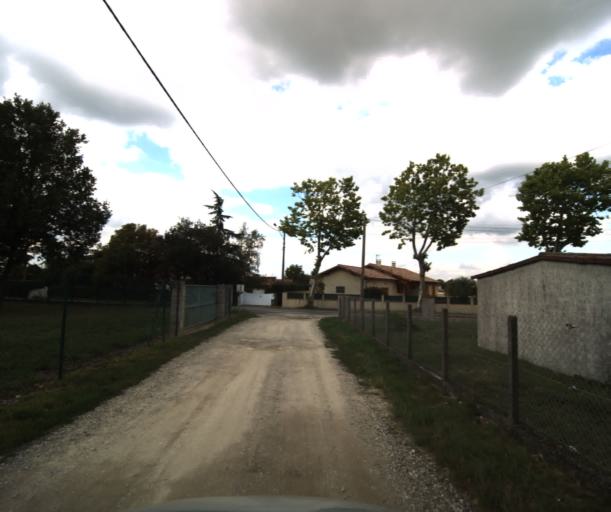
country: FR
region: Midi-Pyrenees
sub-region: Departement de la Haute-Garonne
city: Eaunes
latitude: 43.4236
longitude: 1.3611
